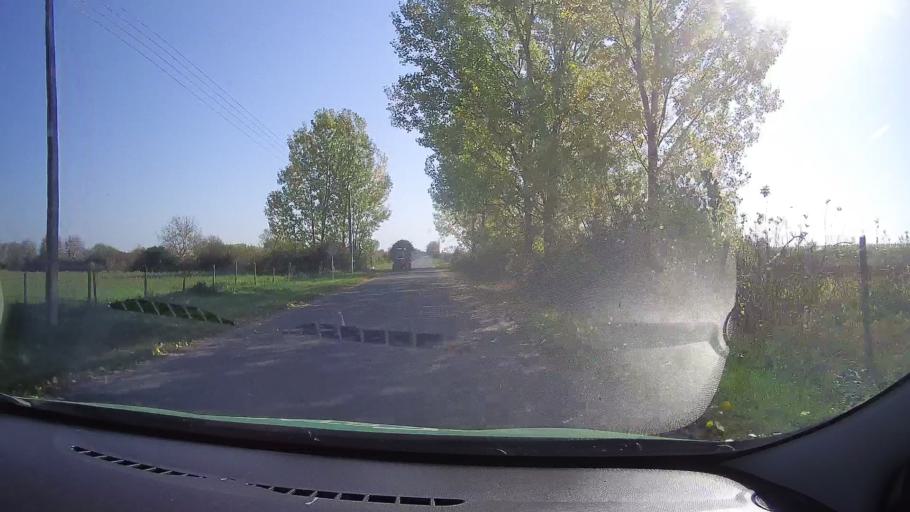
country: RO
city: Foieni
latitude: 47.6974
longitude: 22.3602
